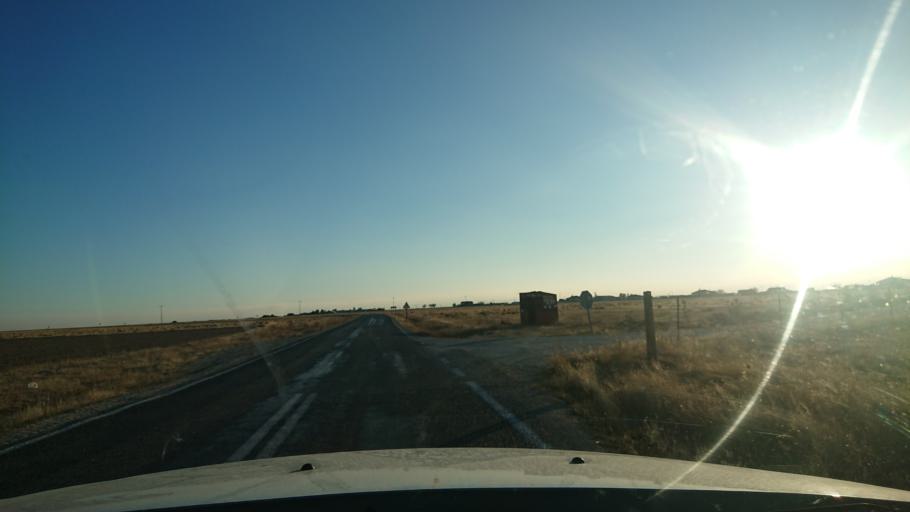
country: TR
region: Aksaray
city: Eskil
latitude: 38.5114
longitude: 33.1983
